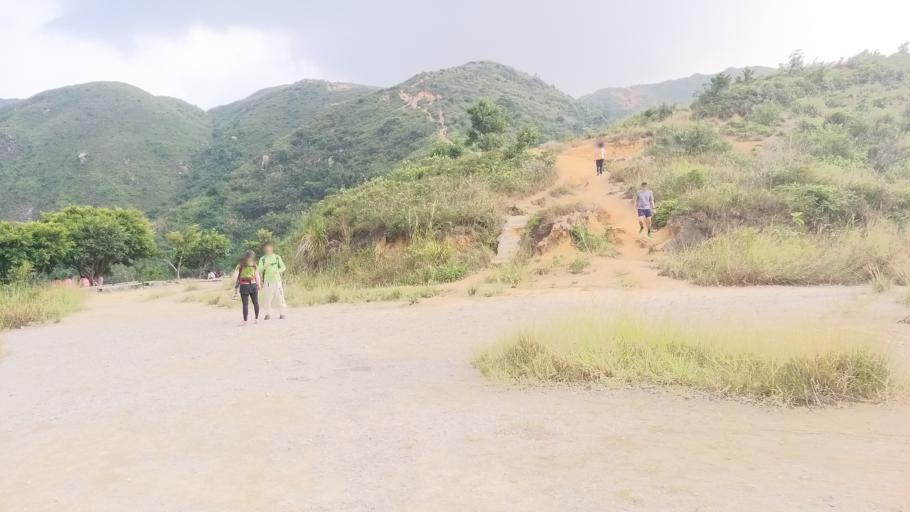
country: HK
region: Tuen Mun
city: Tuen Mun
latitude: 22.4071
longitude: 113.9532
